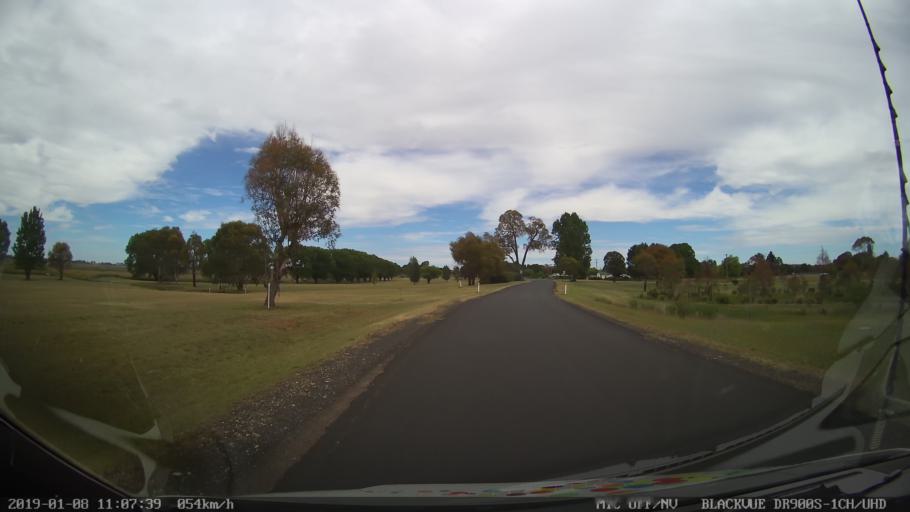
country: AU
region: New South Wales
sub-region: Guyra
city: Guyra
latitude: -30.2171
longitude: 151.6637
